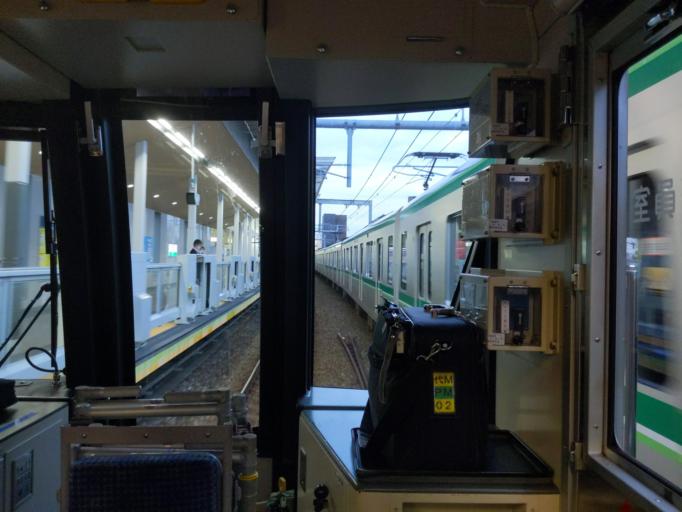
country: JP
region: Saitama
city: Yashio-shi
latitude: 35.7755
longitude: 139.8321
